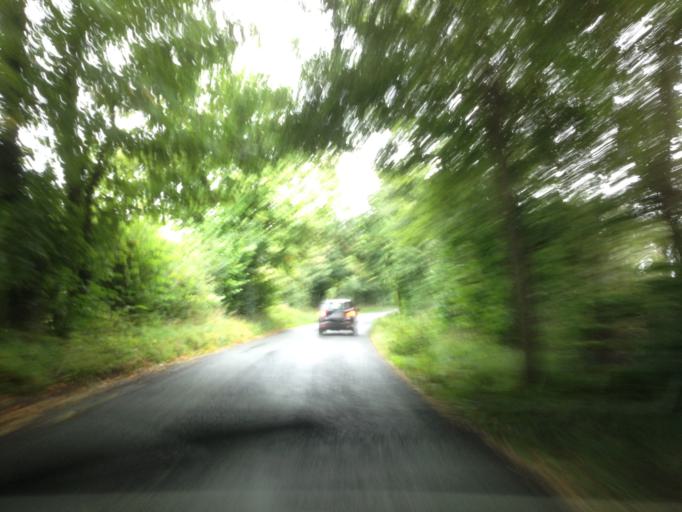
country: FR
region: Lower Normandy
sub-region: Departement du Calvados
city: Saint-Vigor-le-Grand
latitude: 49.3003
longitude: -0.6934
